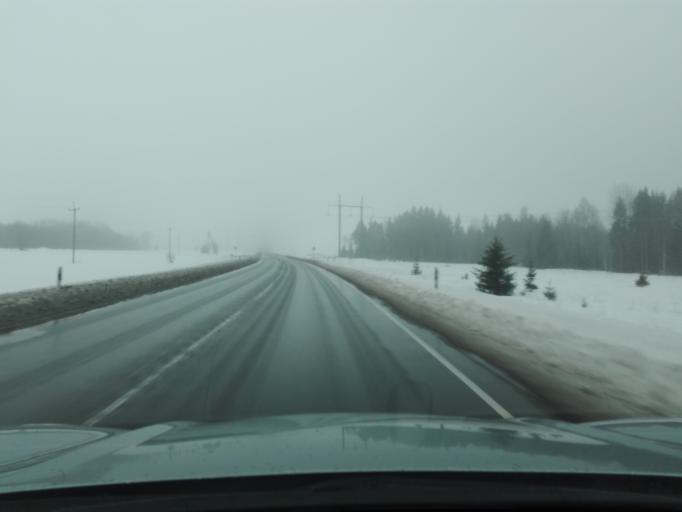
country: EE
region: Raplamaa
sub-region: Kohila vald
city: Kohila
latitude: 59.2157
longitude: 24.7762
